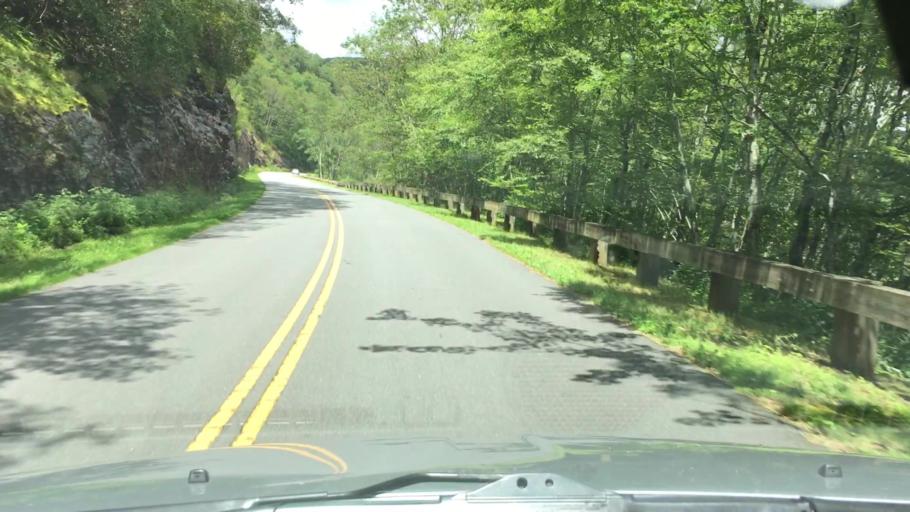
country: US
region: North Carolina
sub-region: Buncombe County
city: Swannanoa
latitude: 35.6888
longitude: -82.4091
